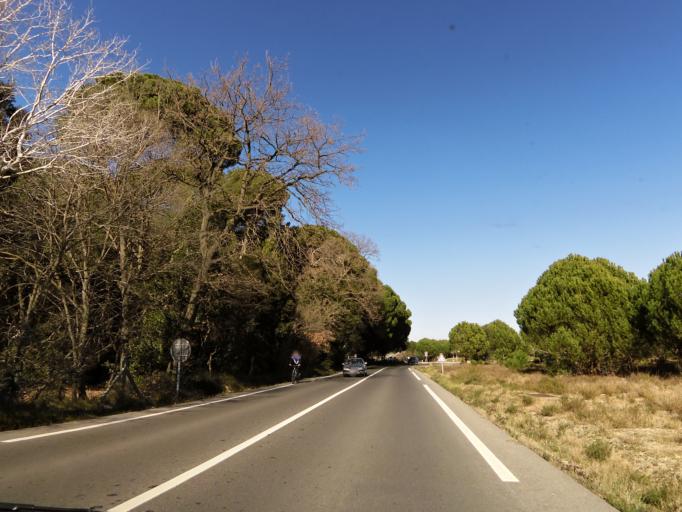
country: FR
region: Languedoc-Roussillon
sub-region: Departement du Gard
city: Aigues-Mortes
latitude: 43.5843
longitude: 4.2087
